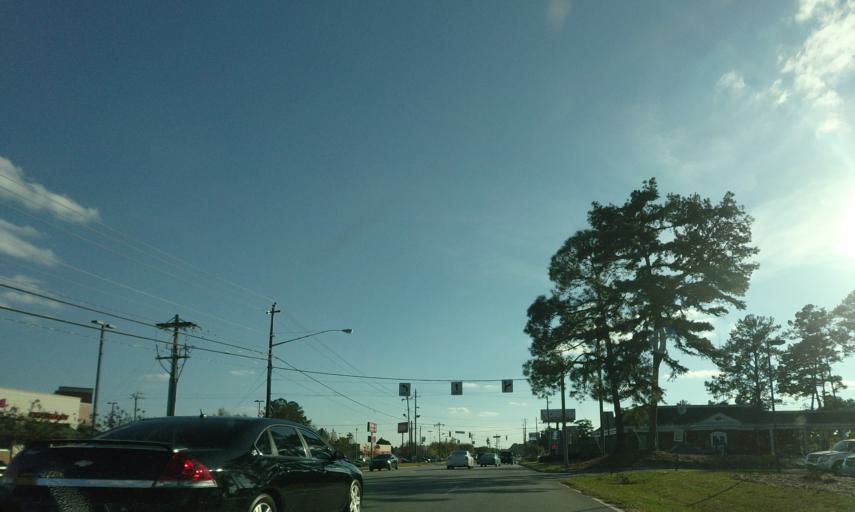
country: US
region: Georgia
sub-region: Lowndes County
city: Remerton
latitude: 30.8479
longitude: -83.3242
